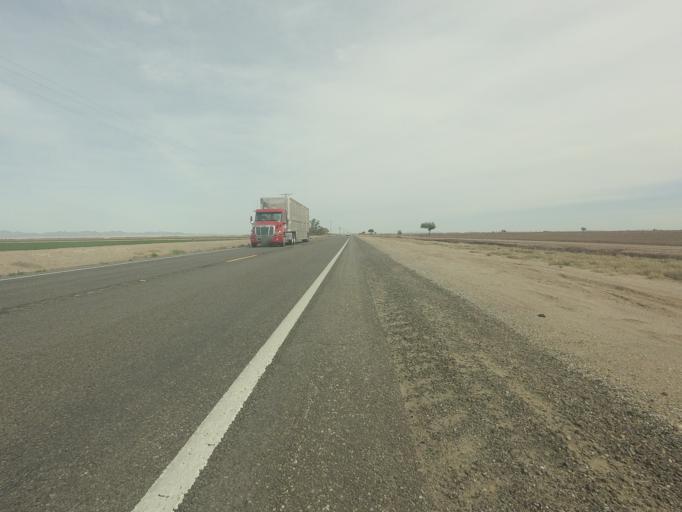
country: US
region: California
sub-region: Imperial County
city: Brawley
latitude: 32.9746
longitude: -115.3693
